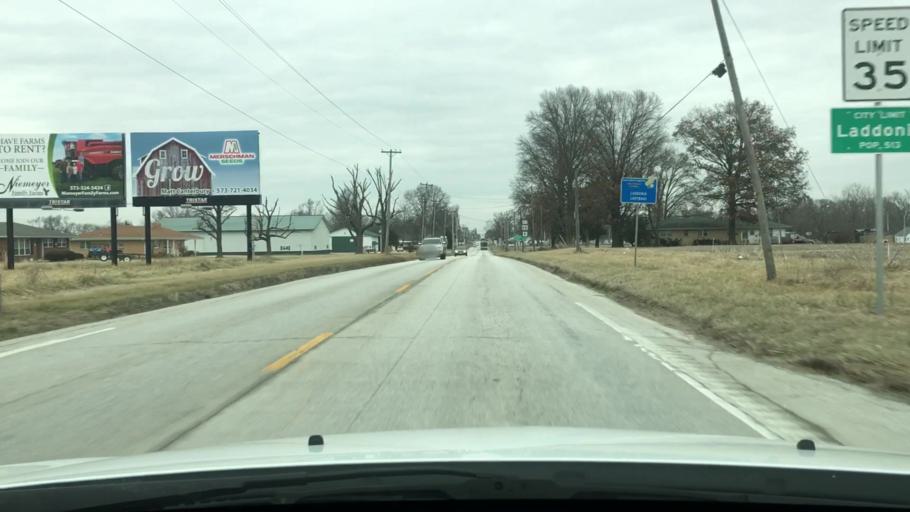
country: US
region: Missouri
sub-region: Audrain County
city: Vandalia
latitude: 39.2345
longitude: -91.6458
